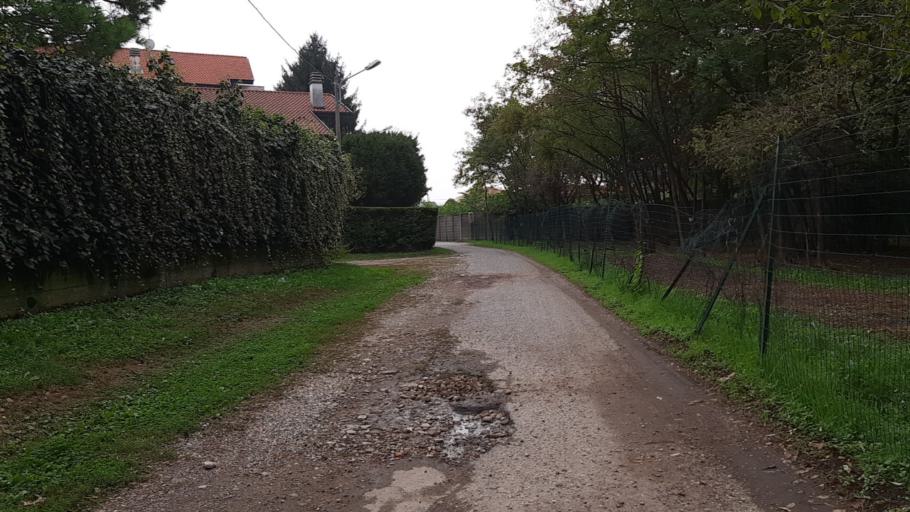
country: IT
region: Lombardy
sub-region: Provincia di Varese
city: Busto Arsizio
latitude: 45.6009
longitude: 8.8511
